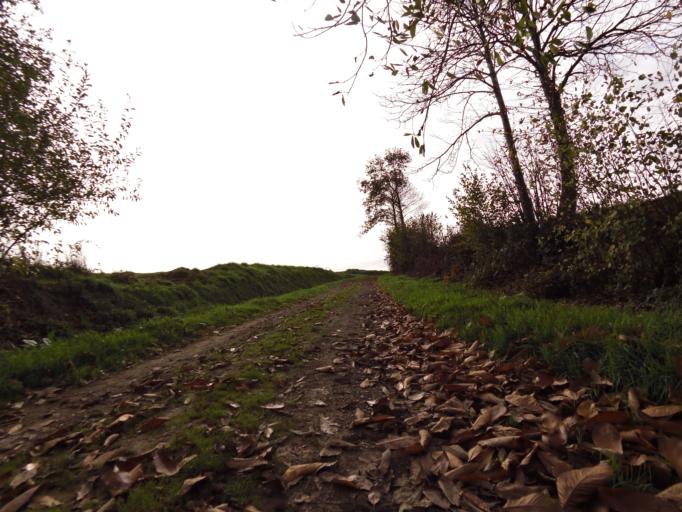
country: FR
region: Brittany
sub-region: Departement d'Ille-et-Vilaine
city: Chanteloup
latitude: 47.9626
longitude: -1.6486
